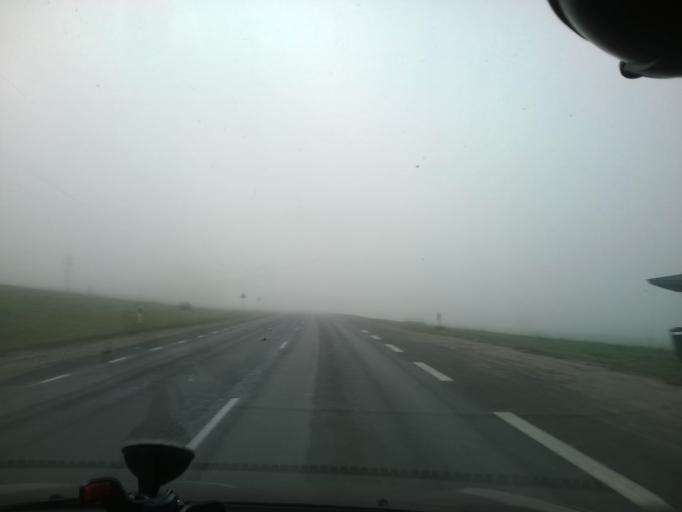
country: EE
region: Tartu
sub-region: Elva linn
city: Elva
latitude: 58.1366
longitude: 26.5207
